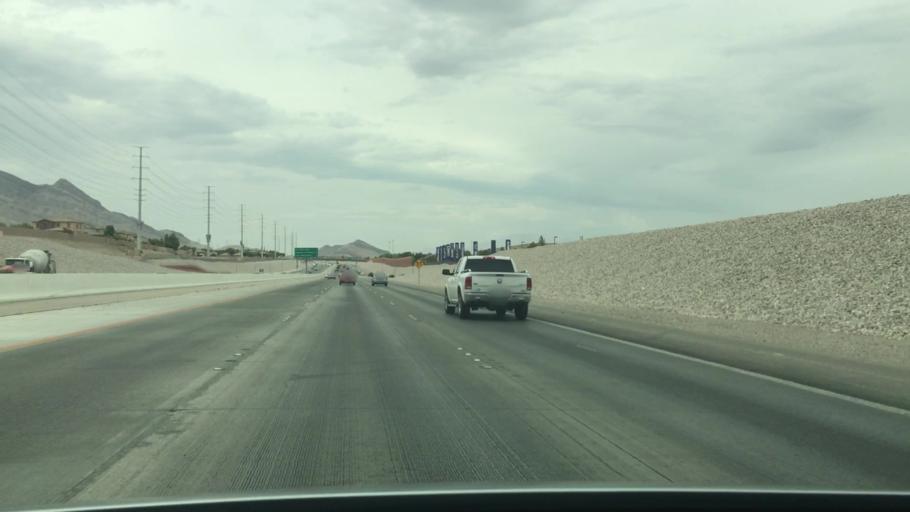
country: US
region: Nevada
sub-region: Clark County
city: Summerlin South
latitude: 36.1595
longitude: -115.3371
